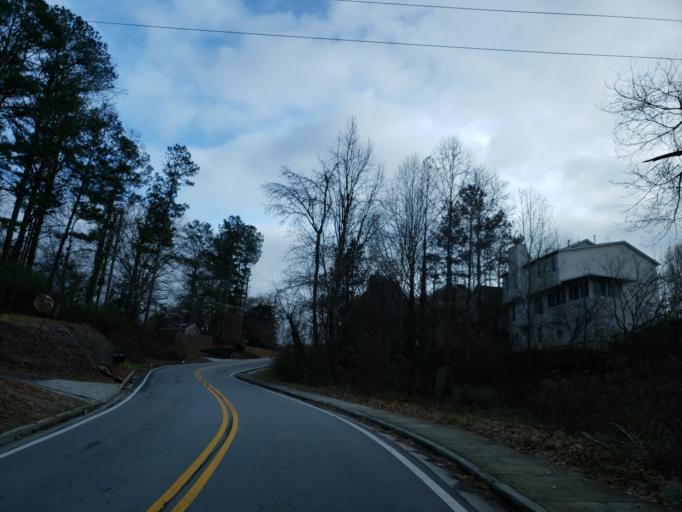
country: US
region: Georgia
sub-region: Cobb County
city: Fair Oaks
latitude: 33.9075
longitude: -84.5680
